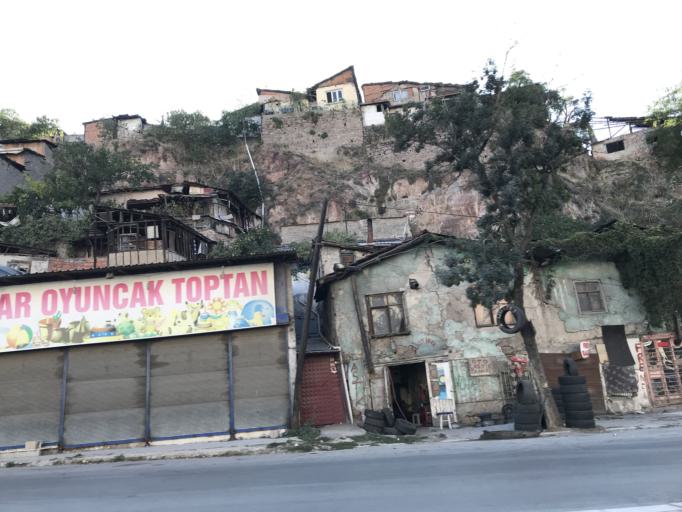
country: TR
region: Ankara
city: Cankaya
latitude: 39.9406
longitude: 32.8718
